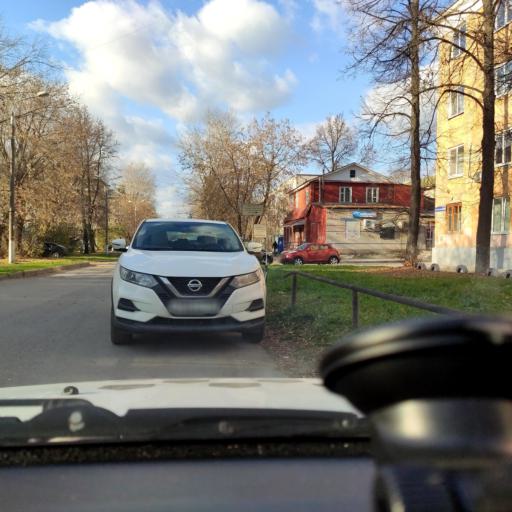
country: RU
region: Perm
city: Perm
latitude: 58.0101
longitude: 56.2028
